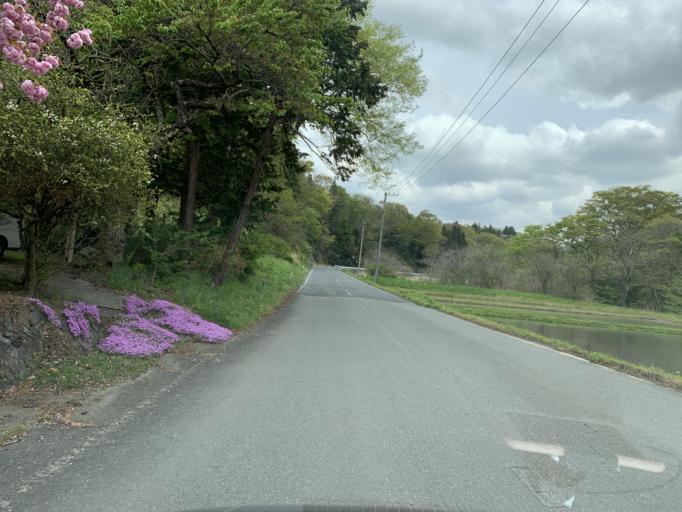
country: JP
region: Iwate
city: Ichinoseki
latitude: 38.8417
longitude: 141.3464
